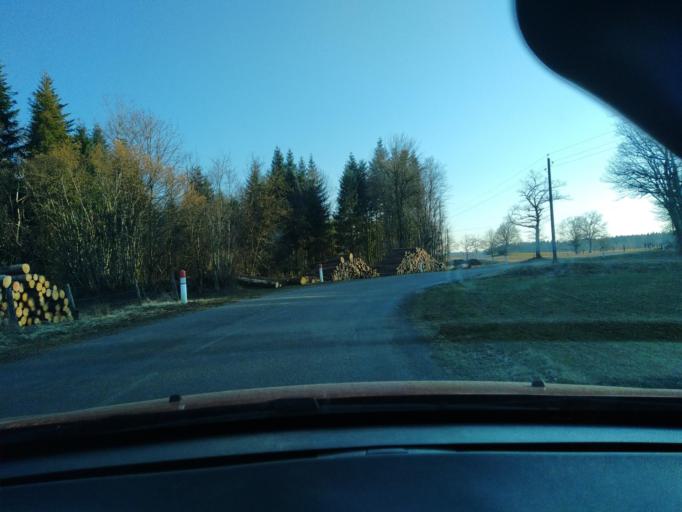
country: FR
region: Franche-Comte
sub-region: Departement du Jura
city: Perrigny
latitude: 46.6539
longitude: 5.6443
